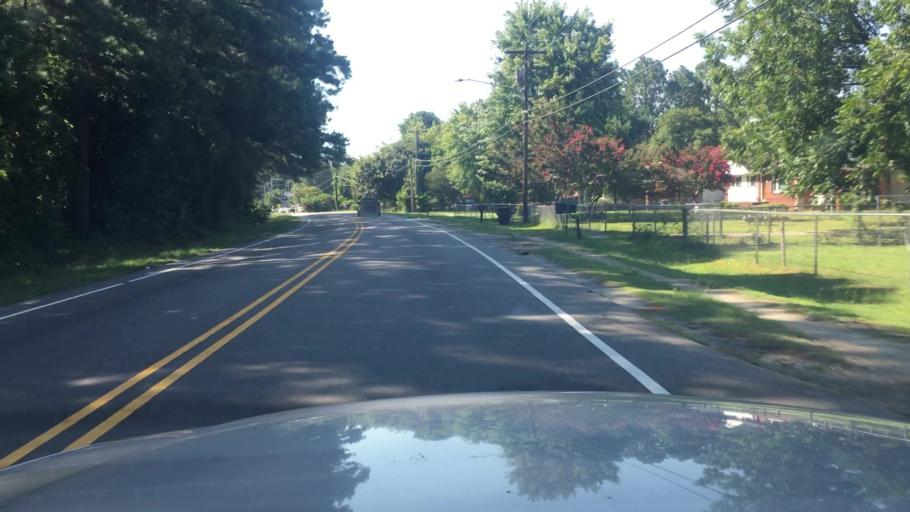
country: US
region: North Carolina
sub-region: Cumberland County
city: Fayetteville
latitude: 35.1057
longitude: -78.9014
